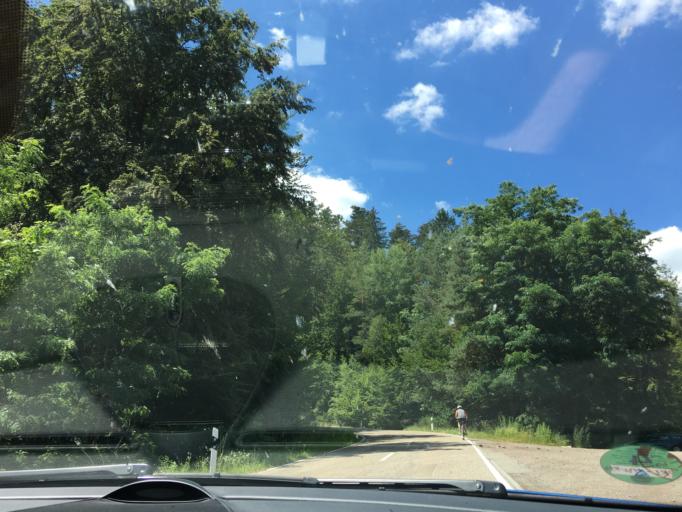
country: DE
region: Rheinland-Pfalz
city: Hauenstein
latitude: 49.2040
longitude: 7.8532
